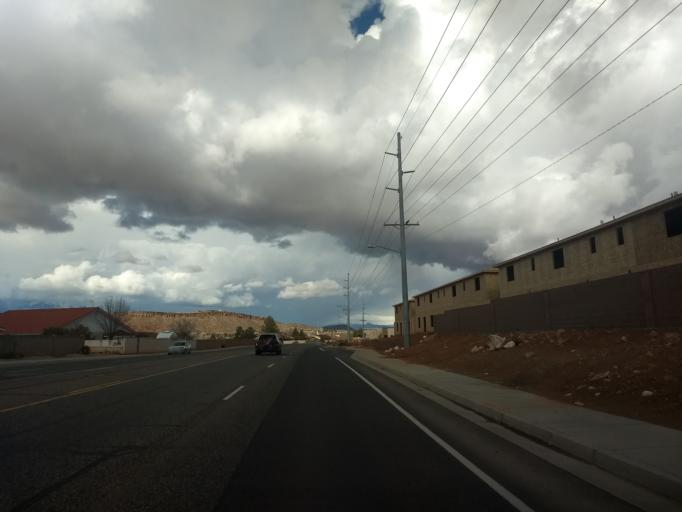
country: US
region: Utah
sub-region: Washington County
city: Saint George
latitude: 37.0554
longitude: -113.5522
